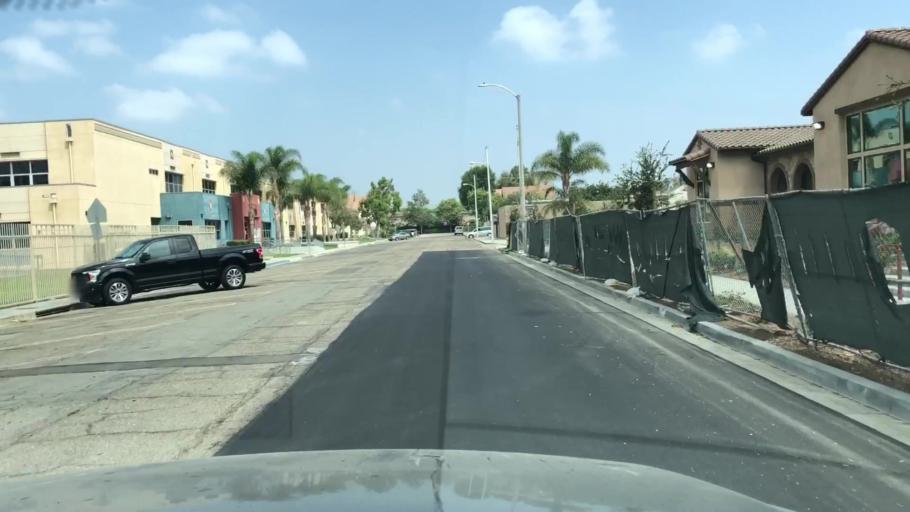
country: US
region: California
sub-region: Ventura County
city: Oxnard
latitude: 34.2043
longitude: -119.1663
